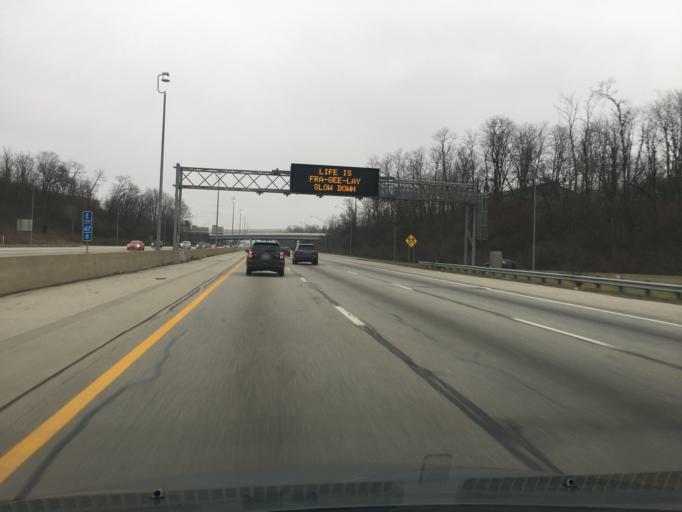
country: US
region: Ohio
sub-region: Hamilton County
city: Highpoint
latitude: 39.2847
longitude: -84.3697
